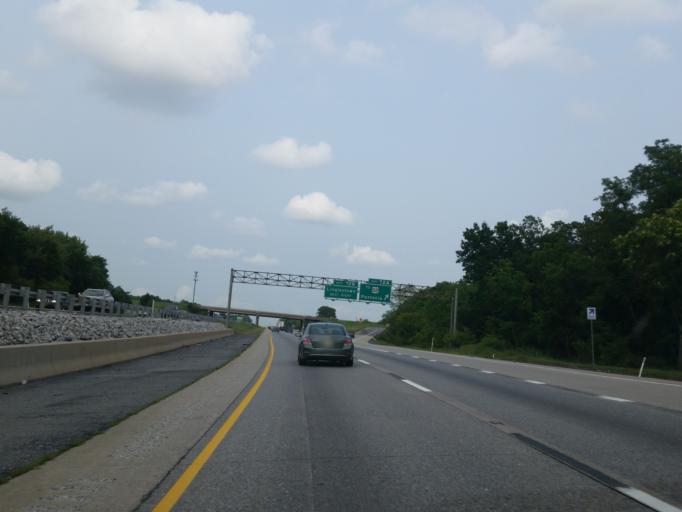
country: US
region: Pennsylvania
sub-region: Dauphin County
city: Paxtonia
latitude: 40.3251
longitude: -76.7959
